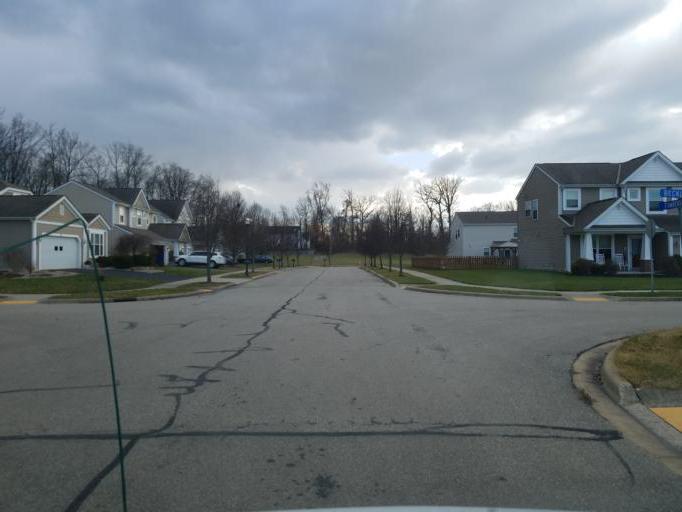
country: US
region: Ohio
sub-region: Delaware County
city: Delaware
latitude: 40.3187
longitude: -83.1046
